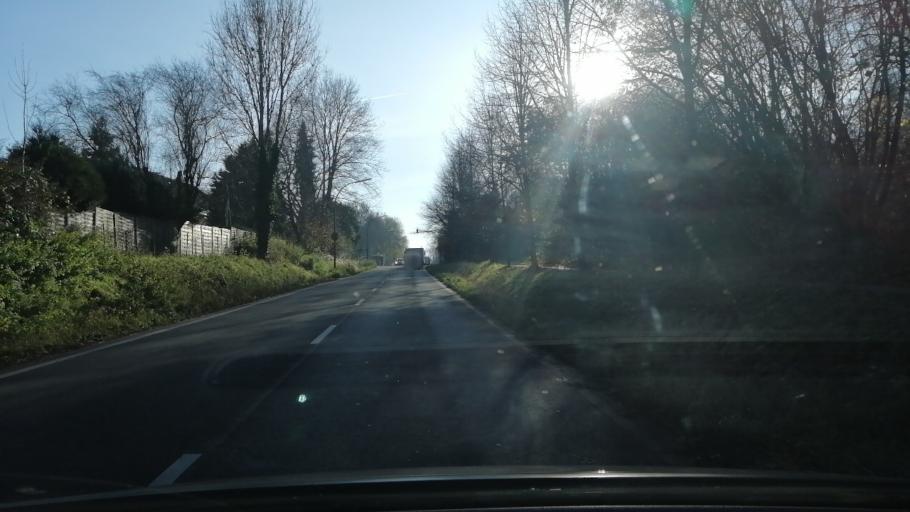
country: DE
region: North Rhine-Westphalia
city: Lanstrop
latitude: 51.5136
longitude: 7.5535
